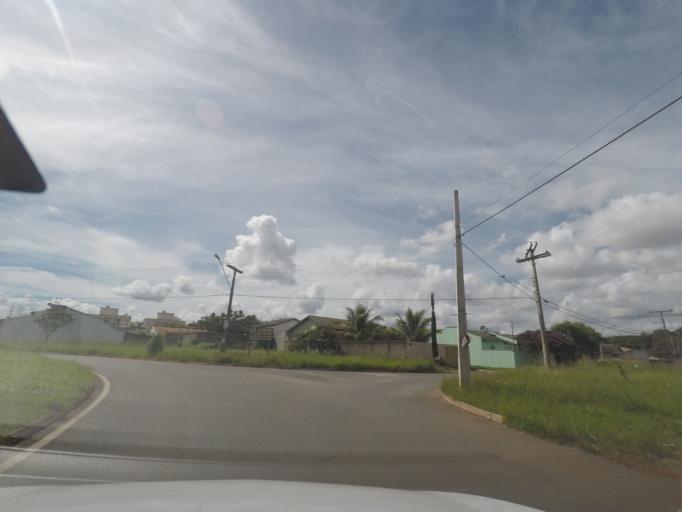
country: BR
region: Goias
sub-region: Goiania
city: Goiania
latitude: -16.7182
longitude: -49.3437
